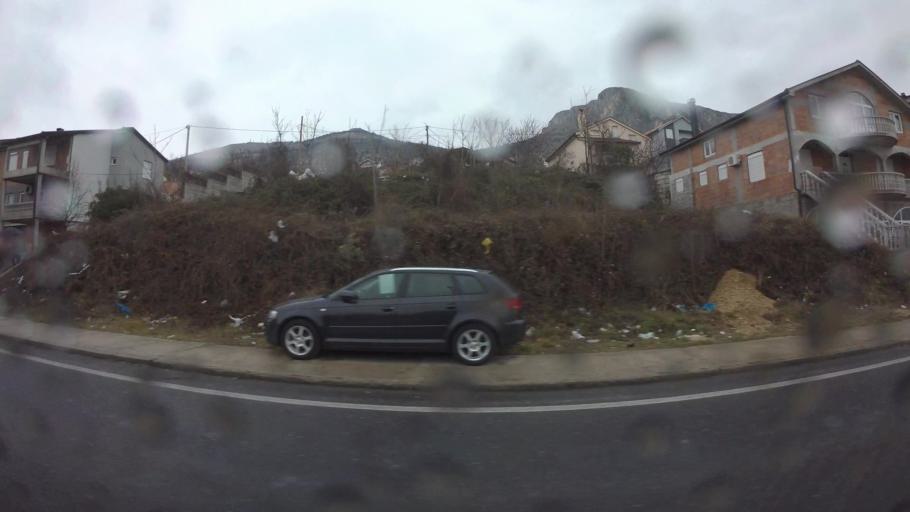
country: BA
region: Federation of Bosnia and Herzegovina
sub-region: Hercegovacko-Bosanski Kanton
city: Mostar
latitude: 43.3456
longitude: 17.8171
